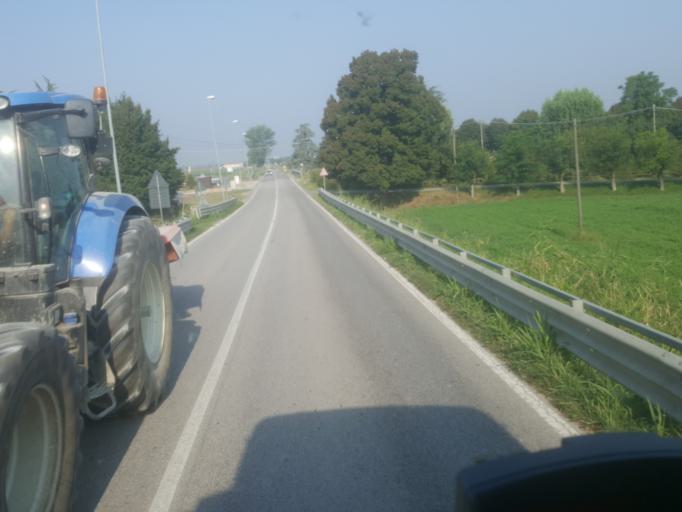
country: IT
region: Emilia-Romagna
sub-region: Provincia di Ravenna
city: Voltana
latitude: 44.5555
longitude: 11.9322
